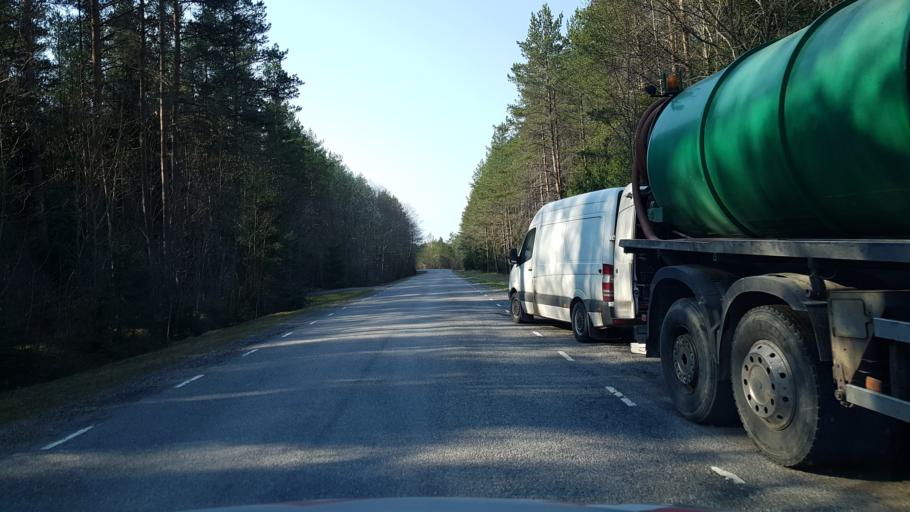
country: EE
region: Raplamaa
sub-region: Kohila vald
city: Kohila
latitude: 59.1970
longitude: 24.6661
